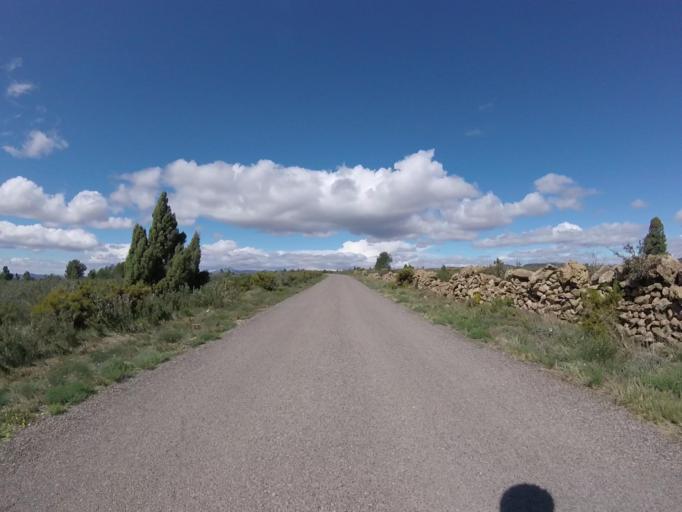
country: ES
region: Valencia
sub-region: Provincia de Castello
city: Culla
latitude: 40.3062
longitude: -0.1118
